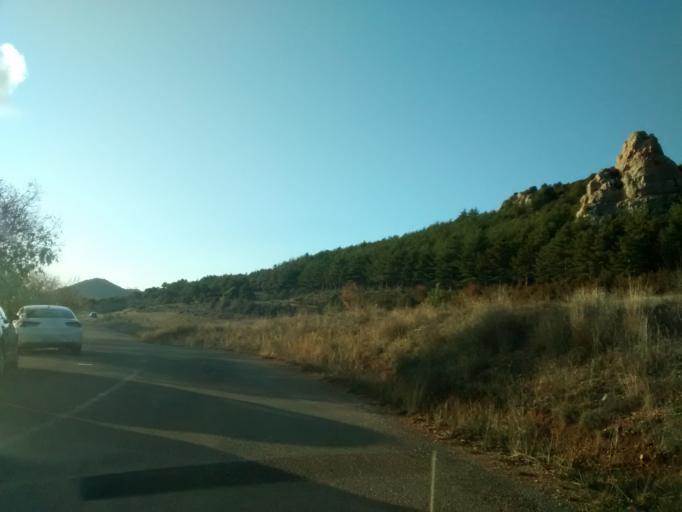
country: ES
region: Aragon
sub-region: Provincia de Huesca
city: Loarre
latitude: 42.3281
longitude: -0.6100
